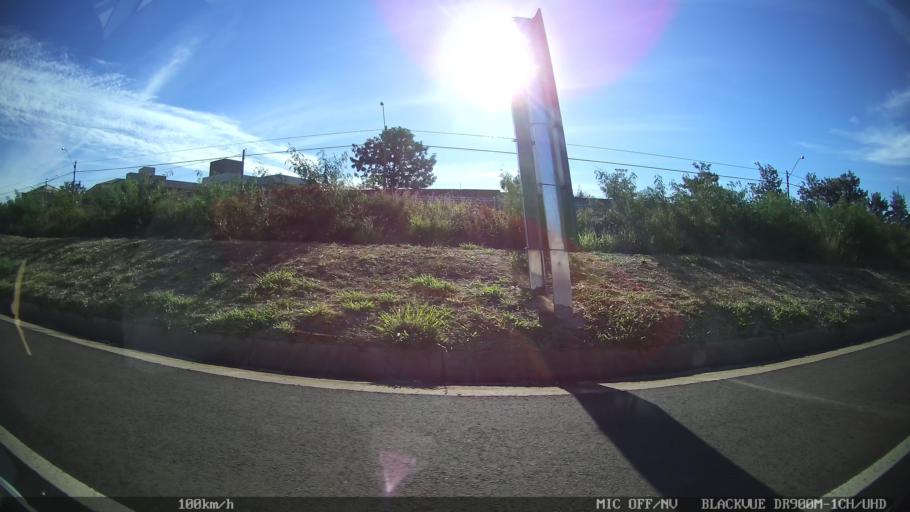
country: BR
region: Sao Paulo
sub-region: Sao Jose Do Rio Preto
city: Sao Jose do Rio Preto
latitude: -20.8612
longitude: -49.4091
